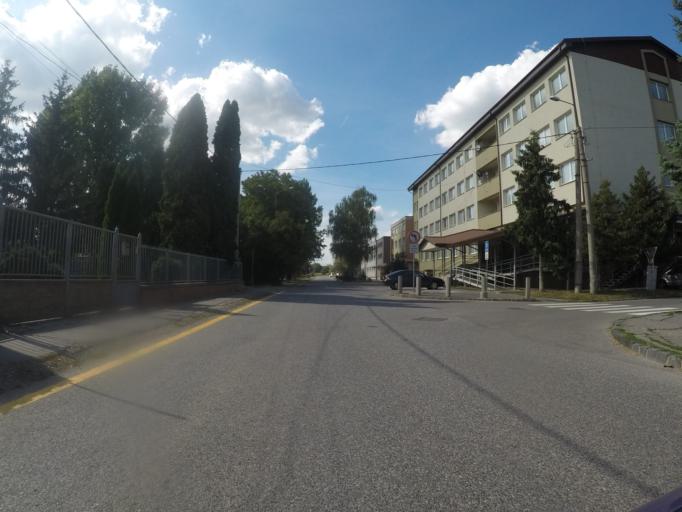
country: SK
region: Banskobystricky
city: Rimavska Sobota
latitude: 48.3880
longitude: 20.0163
